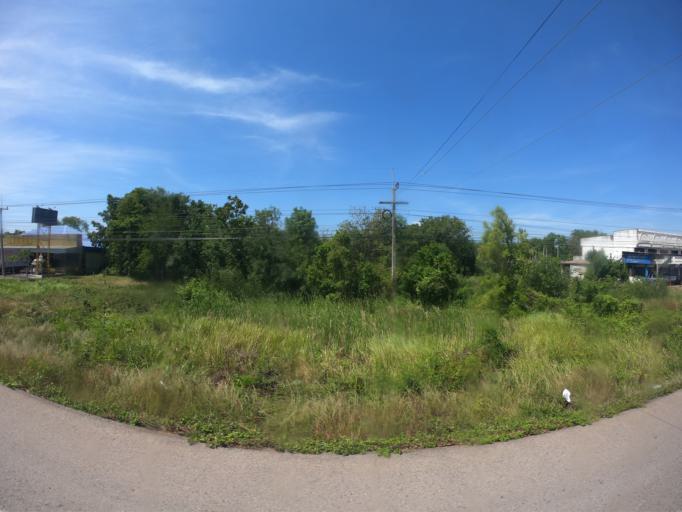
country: TH
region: Nakhon Ratchasima
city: Sida
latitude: 15.5331
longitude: 102.5444
